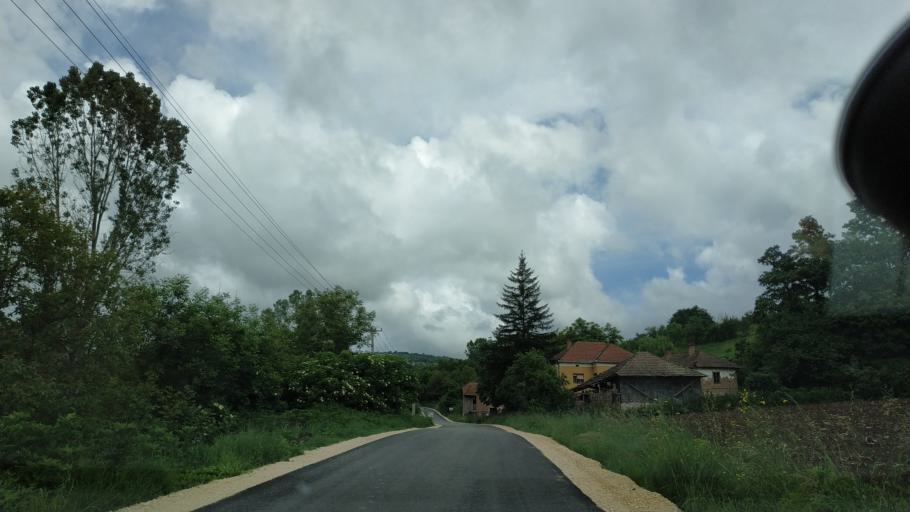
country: RS
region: Central Serbia
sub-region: Zajecarski Okrug
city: Soko Banja
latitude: 43.6697
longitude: 21.9126
